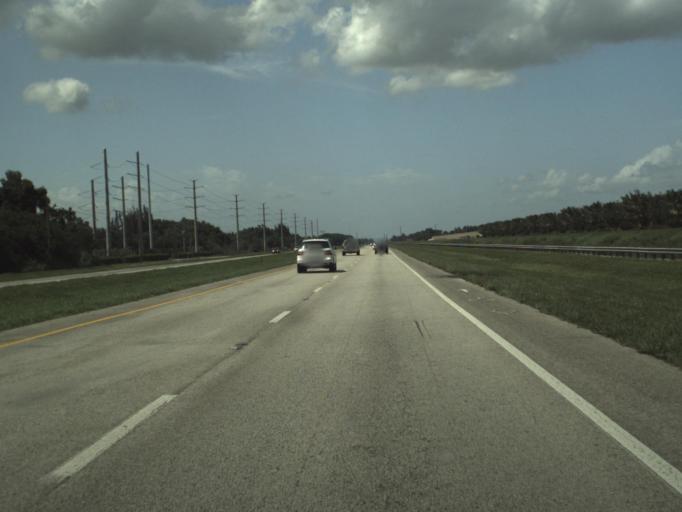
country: US
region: Florida
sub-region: Palm Beach County
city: Villages of Oriole
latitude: 26.4259
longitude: -80.2041
